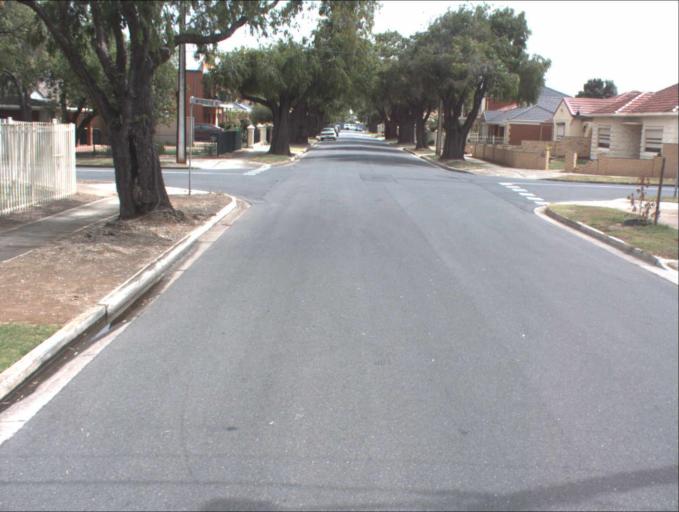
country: AU
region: South Australia
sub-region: Charles Sturt
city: Woodville
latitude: -34.8742
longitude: 138.5584
